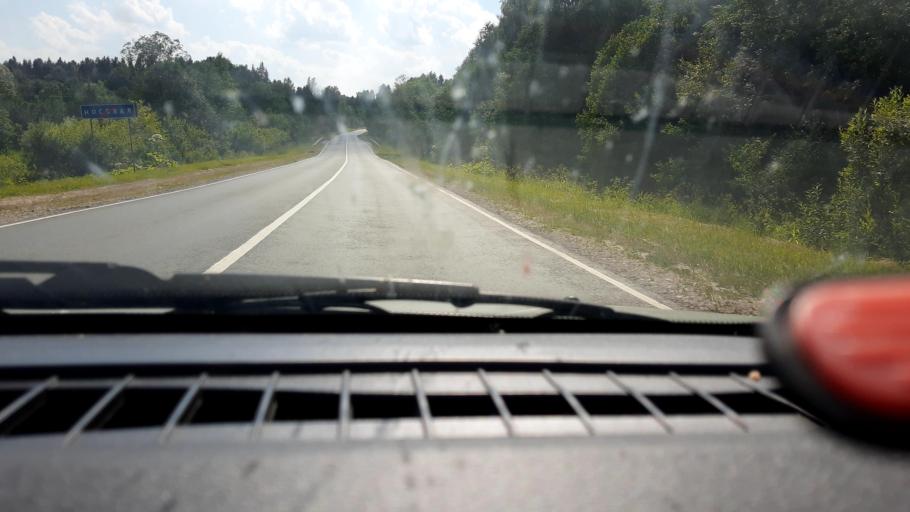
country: RU
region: Nizjnij Novgorod
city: Uren'
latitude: 57.2391
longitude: 45.5653
